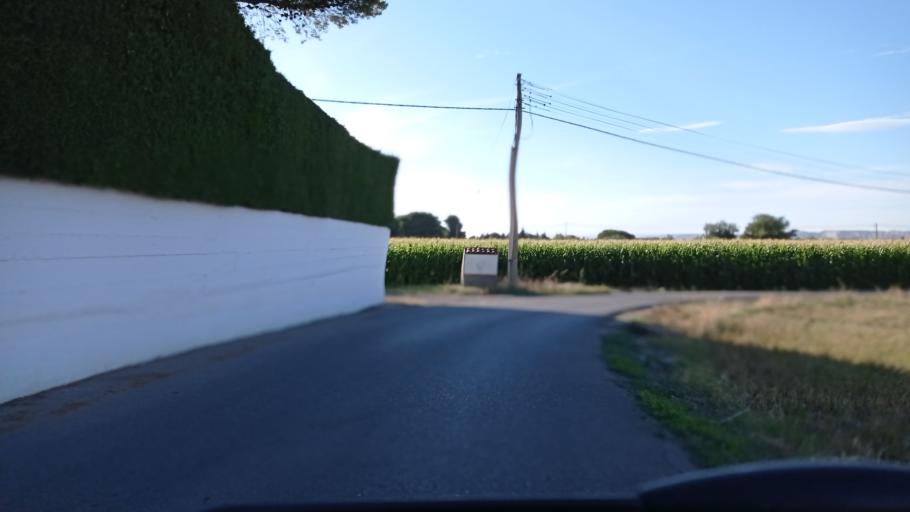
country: ES
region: Aragon
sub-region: Provincia de Zaragoza
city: Oliver-Valdefierro, Oliver, Valdefierro
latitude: 41.6717
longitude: -0.9680
